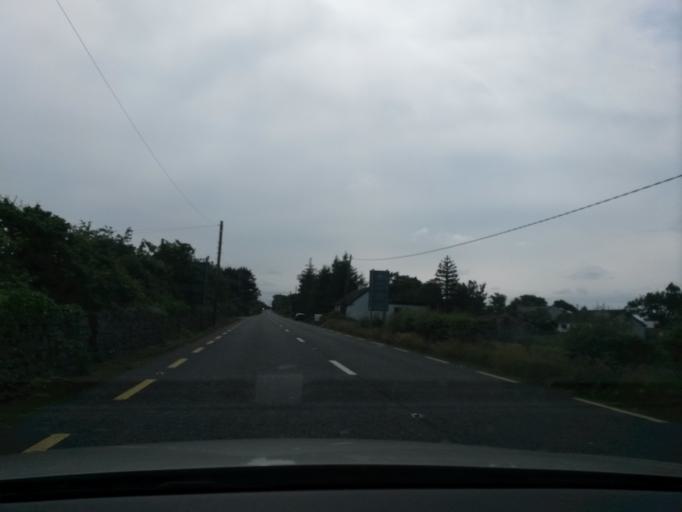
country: IE
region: Connaught
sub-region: Sligo
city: Sligo
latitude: 54.4272
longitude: -8.4610
